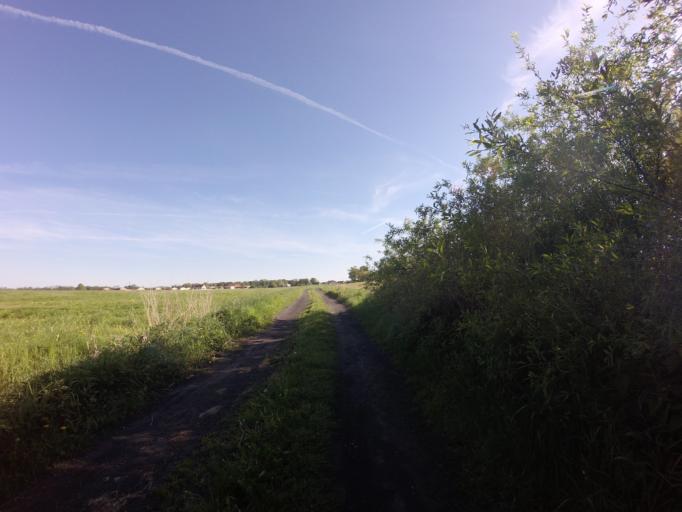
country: PL
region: West Pomeranian Voivodeship
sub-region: Powiat choszczenski
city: Pelczyce
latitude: 53.1251
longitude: 15.3234
